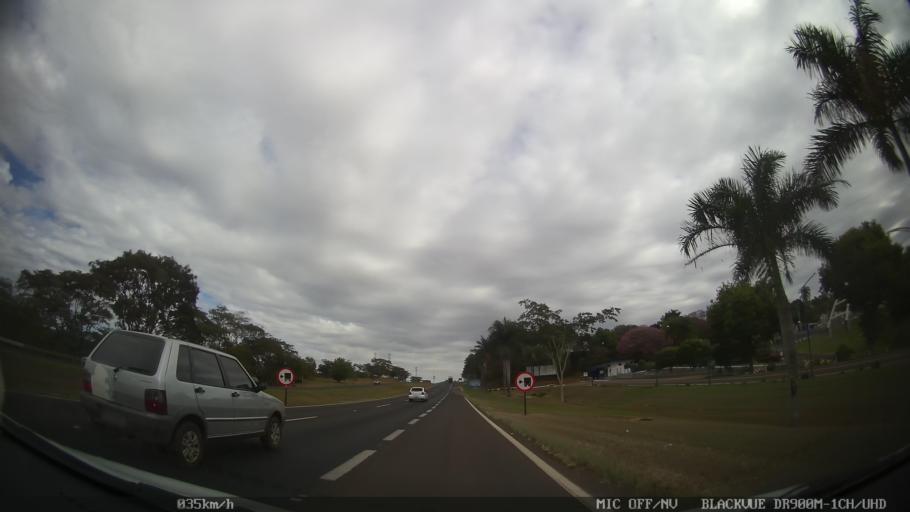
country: BR
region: Sao Paulo
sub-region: Sao Jose Do Rio Preto
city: Sao Jose do Rio Preto
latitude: -20.8157
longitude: -49.4521
